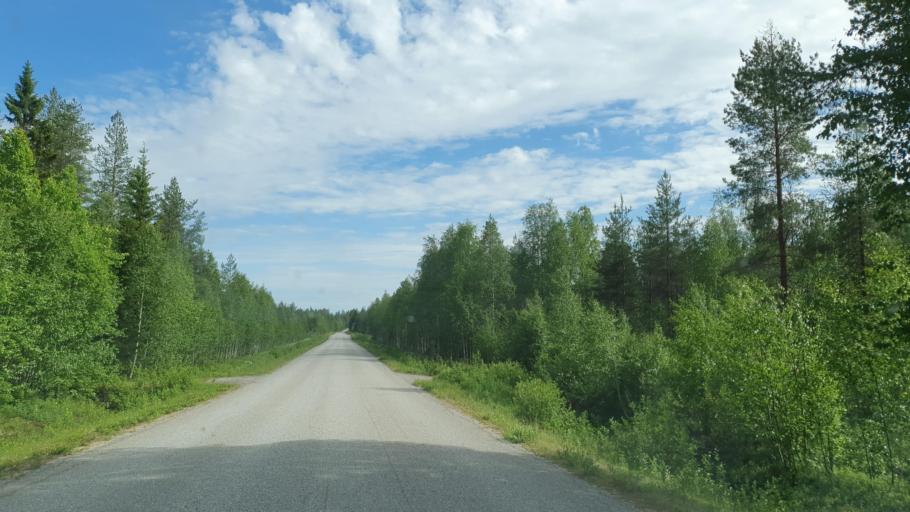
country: FI
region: Kainuu
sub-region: Kehys-Kainuu
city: Suomussalmi
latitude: 64.5881
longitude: 29.1110
